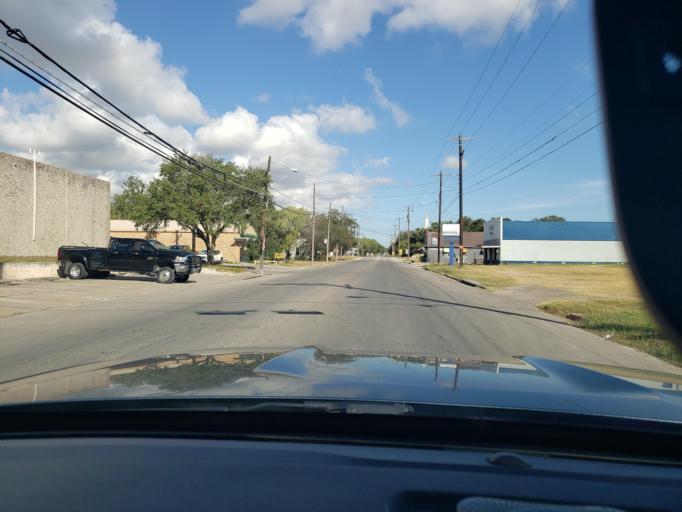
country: US
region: Texas
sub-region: Bee County
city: Beeville
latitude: 28.4050
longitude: -97.7499
